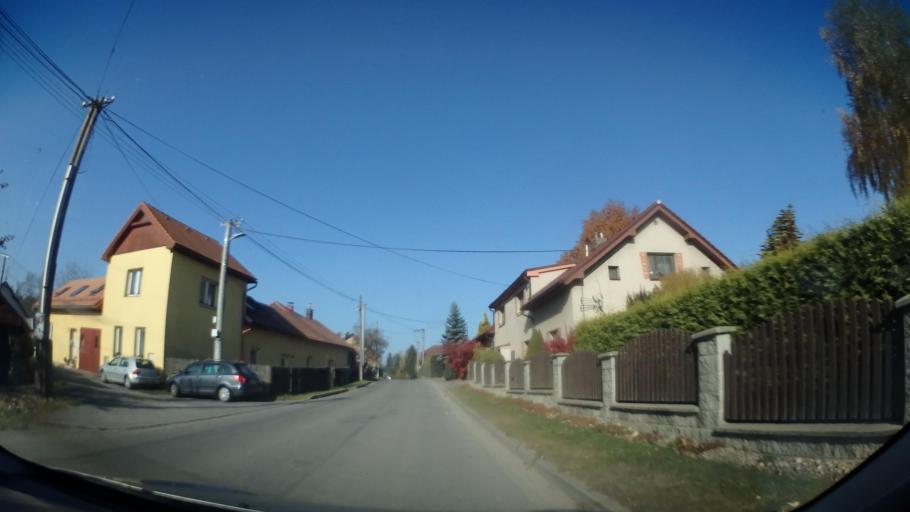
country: CZ
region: Vysocina
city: Zd'ar nad Sazavou Druhy
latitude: 49.6047
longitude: 15.9232
